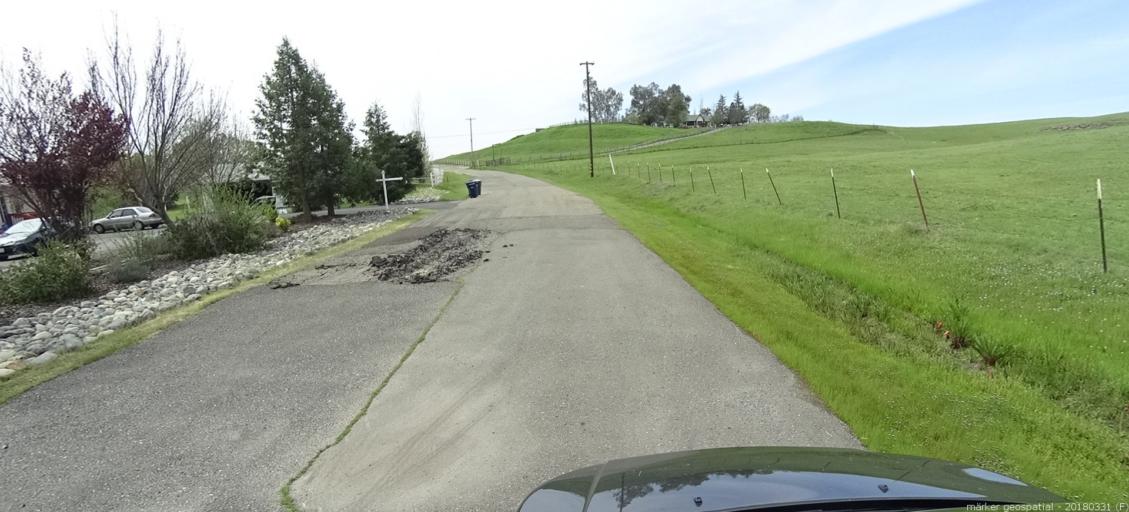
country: US
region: California
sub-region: Sacramento County
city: Rancho Murieta
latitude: 38.5033
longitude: -121.1145
